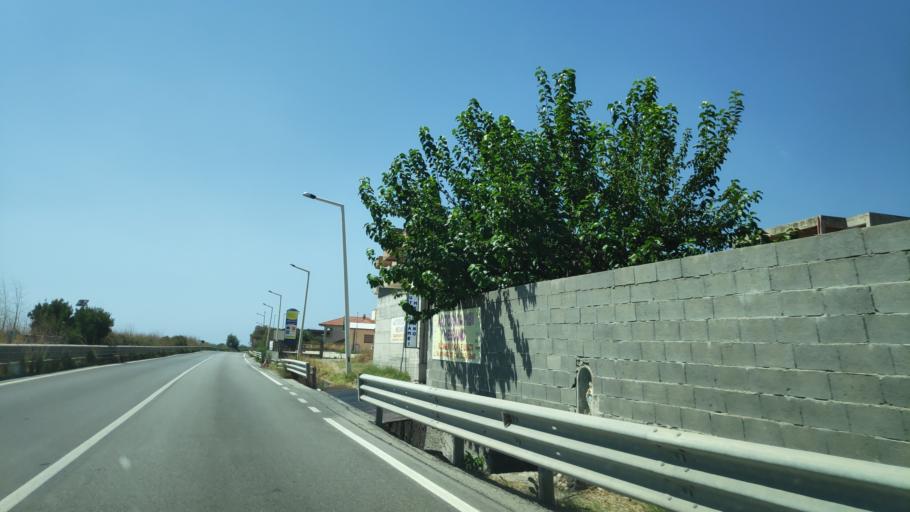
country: IT
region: Calabria
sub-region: Provincia di Reggio Calabria
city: Brancaleone-Marina
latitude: 37.9926
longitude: 16.1210
